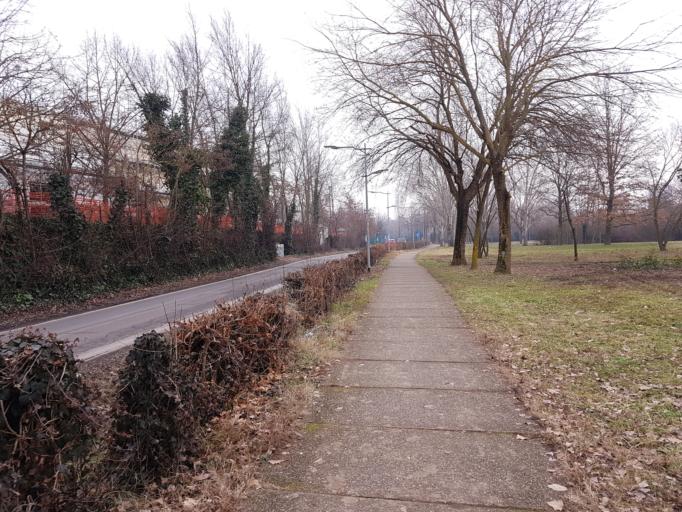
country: IT
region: Emilia-Romagna
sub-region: Provincia di Bologna
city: Quarto Inferiore
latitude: 44.5092
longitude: 11.3849
